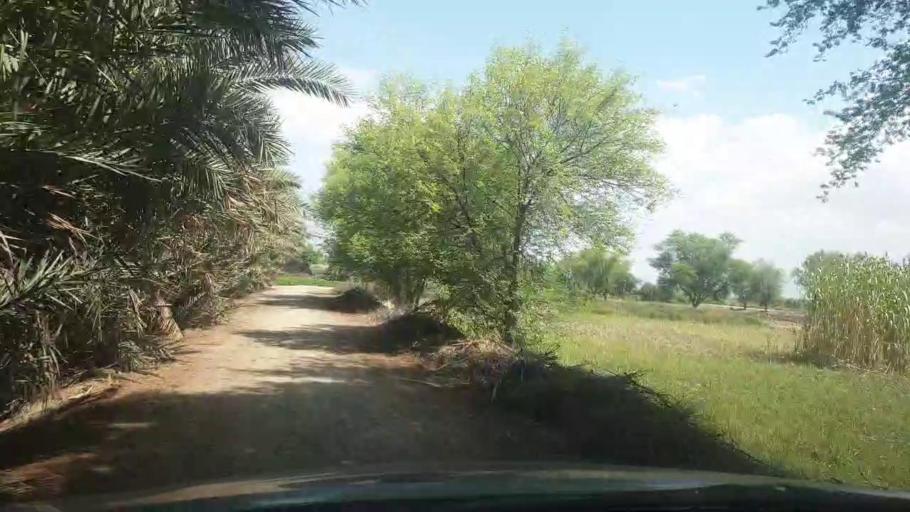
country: PK
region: Sindh
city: Khairpur
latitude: 27.5479
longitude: 68.8021
